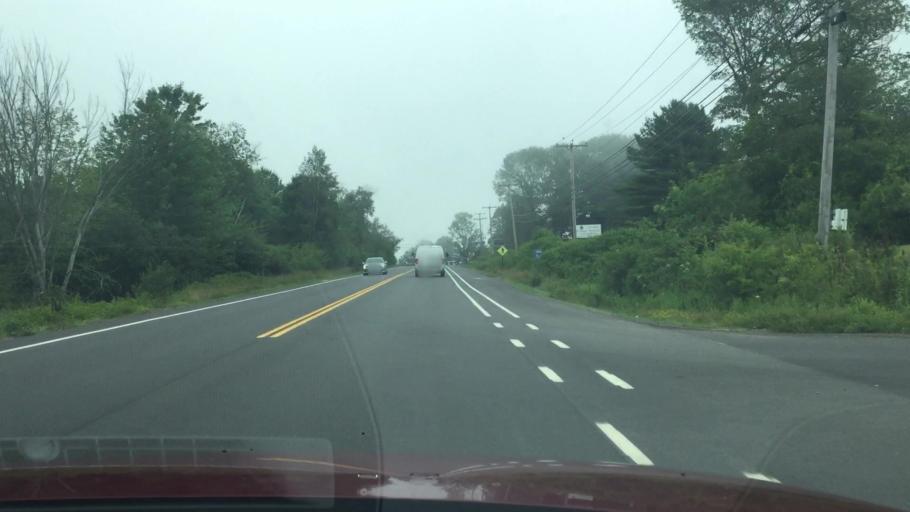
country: US
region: Maine
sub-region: Cumberland County
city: Yarmouth
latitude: 43.8157
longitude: -70.1478
